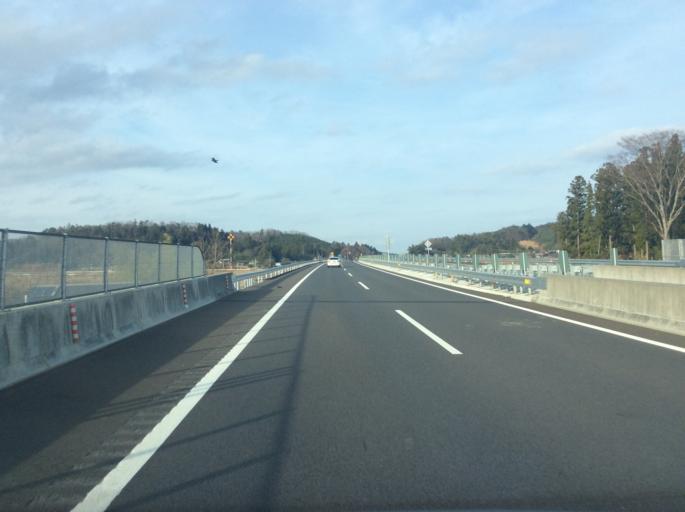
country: JP
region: Fukushima
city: Namie
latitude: 37.4079
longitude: 140.9624
